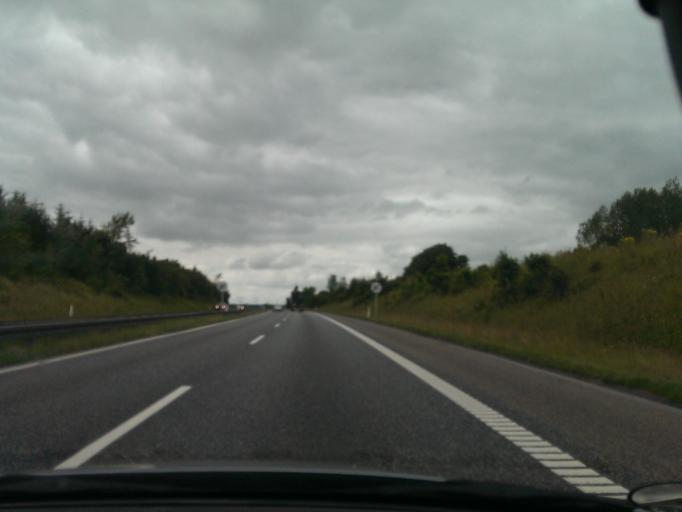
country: DK
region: Central Jutland
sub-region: Arhus Kommune
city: Trige
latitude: 56.2347
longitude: 10.1252
